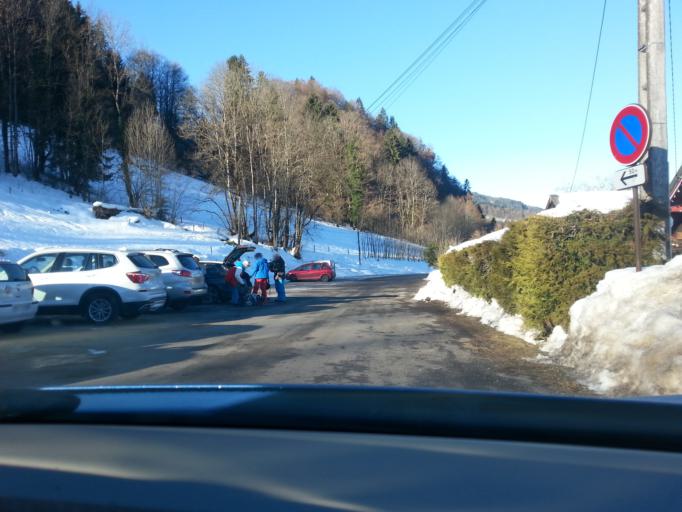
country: FR
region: Rhone-Alpes
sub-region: Departement de la Haute-Savoie
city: Samoens
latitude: 46.0727
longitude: 6.6984
